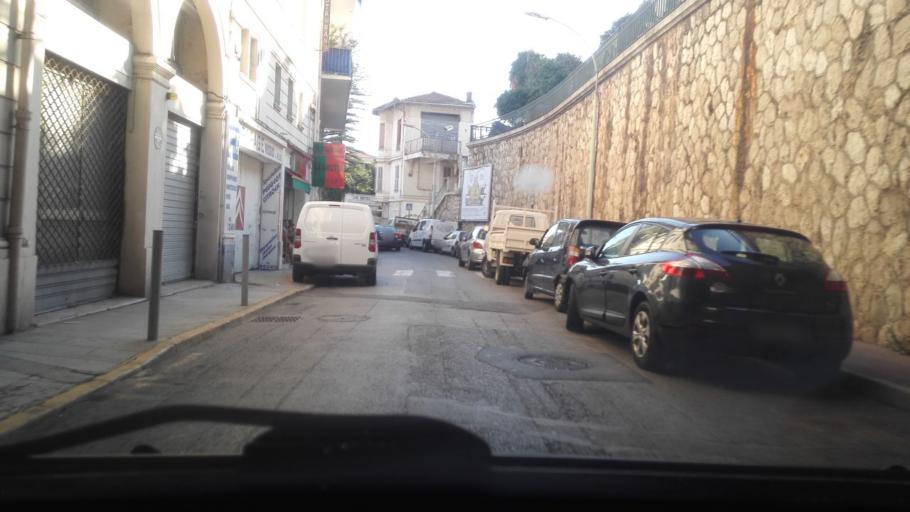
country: FR
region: Provence-Alpes-Cote d'Azur
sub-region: Departement des Alpes-Maritimes
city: Menton
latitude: 43.7747
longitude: 7.4941
